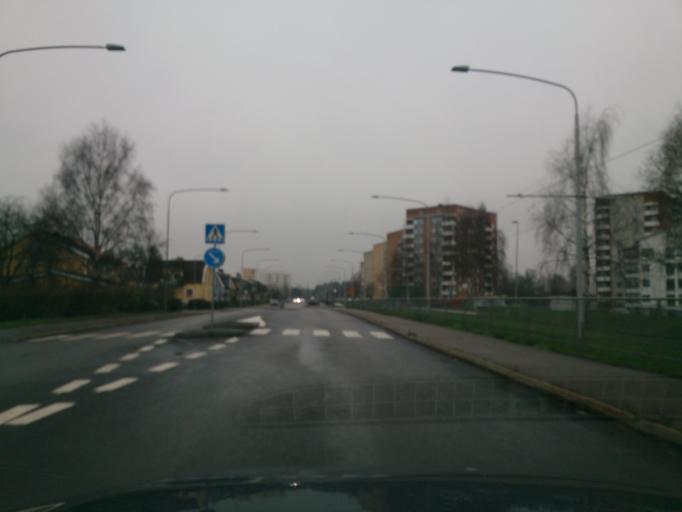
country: SE
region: OEstergoetland
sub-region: Norrkopings Kommun
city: Norrkoping
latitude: 58.6057
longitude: 16.1556
